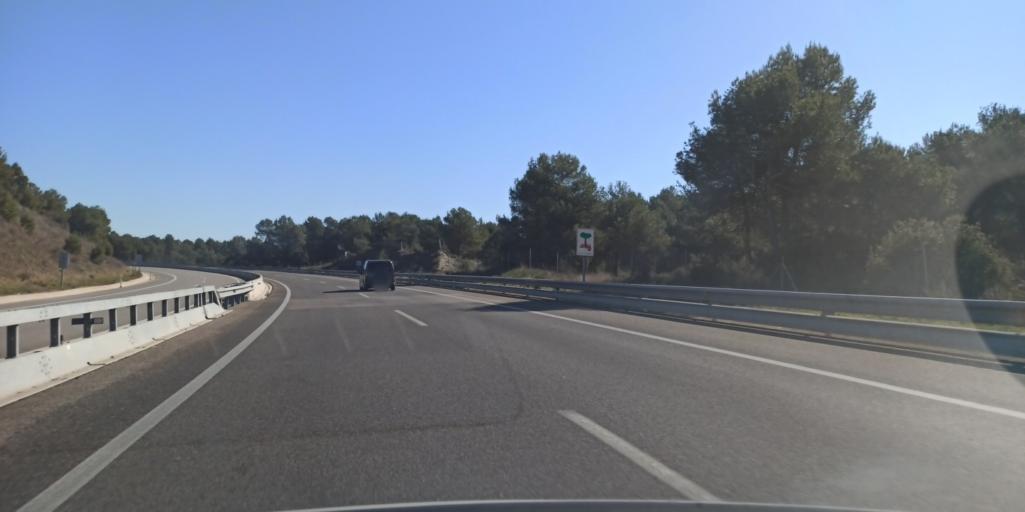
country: ES
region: Catalonia
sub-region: Provincia de Barcelona
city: Avinyo
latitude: 41.8573
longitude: 1.9927
